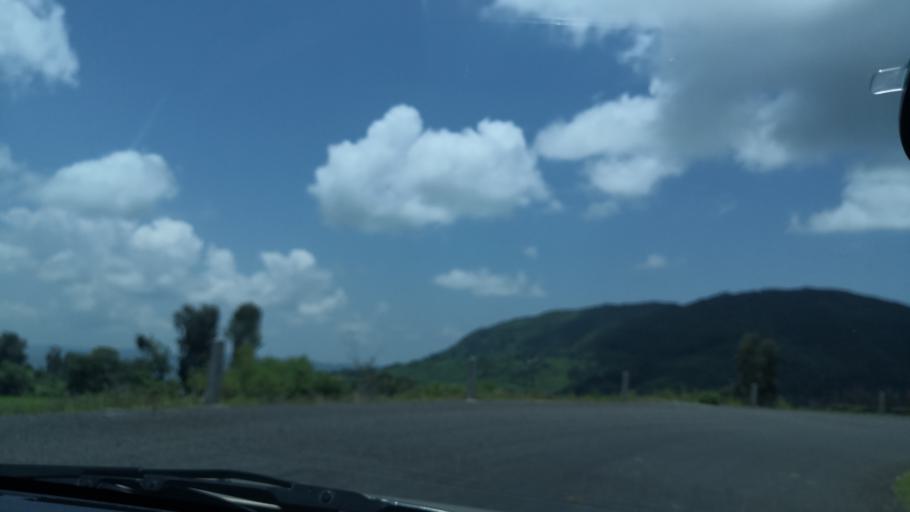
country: ET
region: Amhara
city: Abomsa
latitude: 10.3214
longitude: 39.8729
